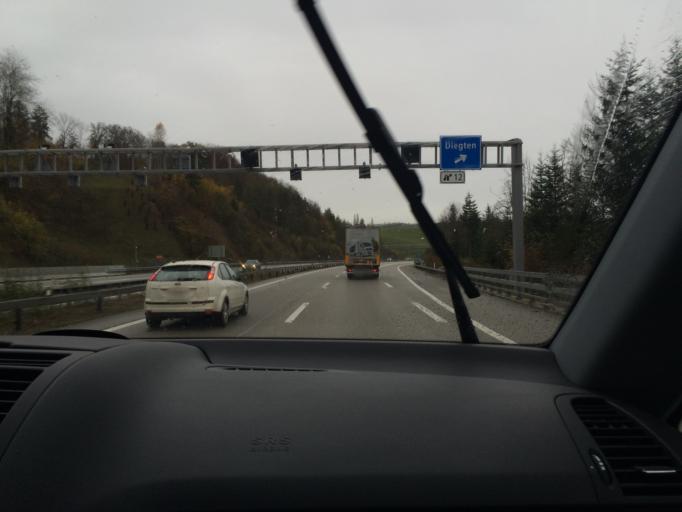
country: CH
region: Basel-Landschaft
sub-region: Bezirk Waldenburg
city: Diegten
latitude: 47.3990
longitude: 7.8108
